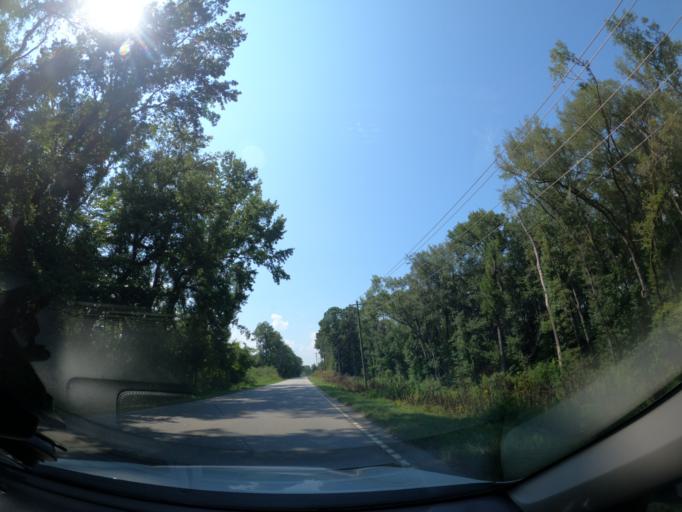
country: US
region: South Carolina
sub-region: Richland County
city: Hopkins
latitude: 33.9240
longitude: -80.9584
